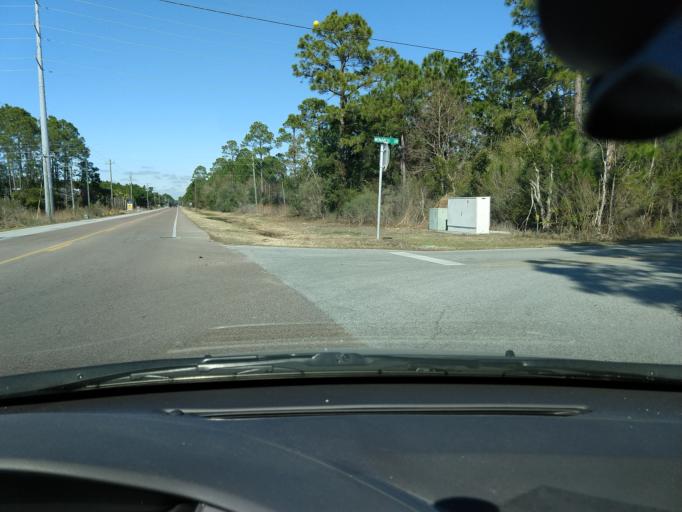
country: US
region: Florida
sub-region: Walton County
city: Miramar Beach
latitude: 30.3793
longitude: -86.3048
